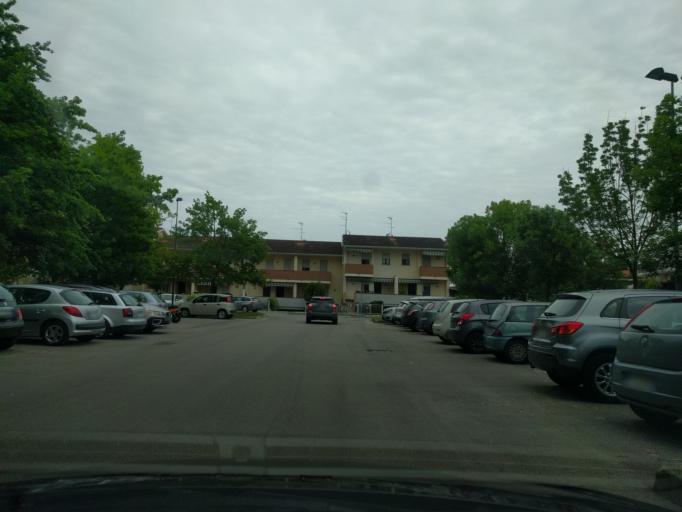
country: IT
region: Veneto
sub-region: Provincia di Rovigo
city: Rovigo
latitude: 45.0598
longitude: 11.7878
